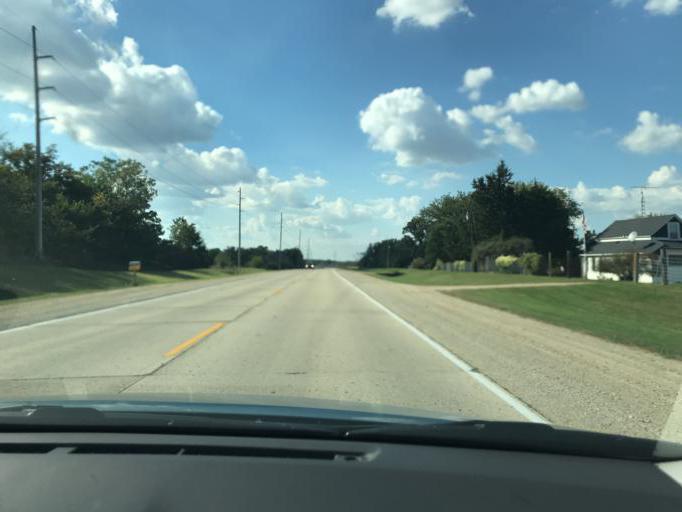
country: US
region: Wisconsin
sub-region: Rock County
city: Orfordville
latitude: 42.5531
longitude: -89.2807
